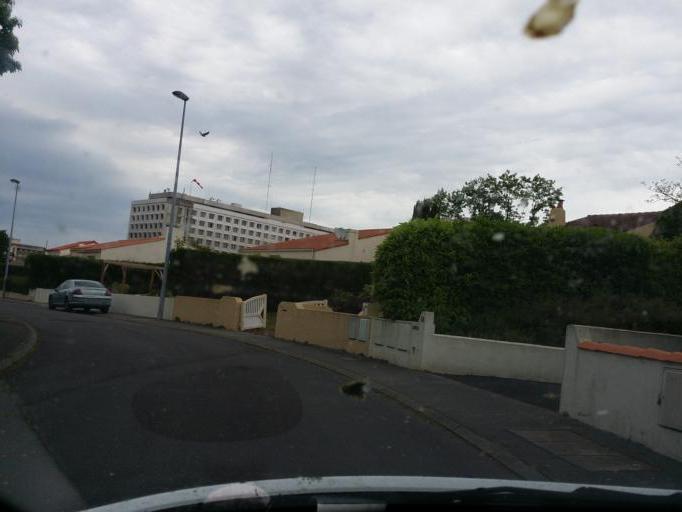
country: FR
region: Pays de la Loire
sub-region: Departement de la Vendee
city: La Roche-sur-Yon
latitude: 46.6662
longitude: -1.4112
